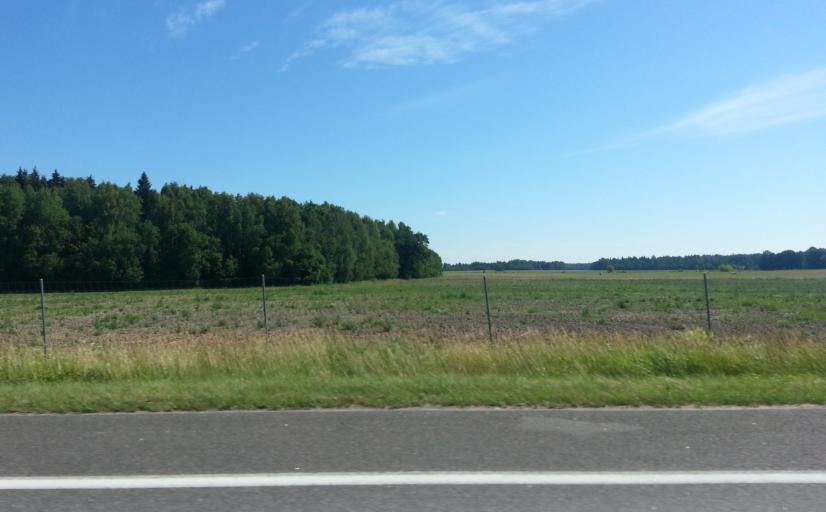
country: LT
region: Vilnius County
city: Ukmerge
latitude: 55.5084
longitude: 24.6097
